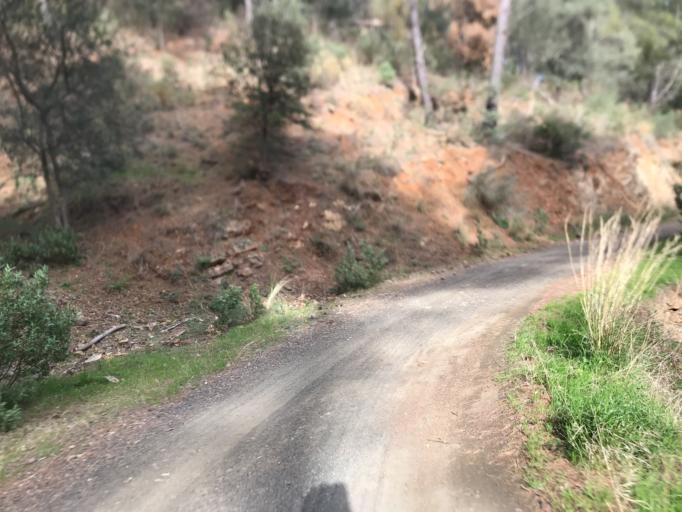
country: ES
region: Andalusia
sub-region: Provincia de Malaga
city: Malaga
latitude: 36.8051
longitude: -4.4005
